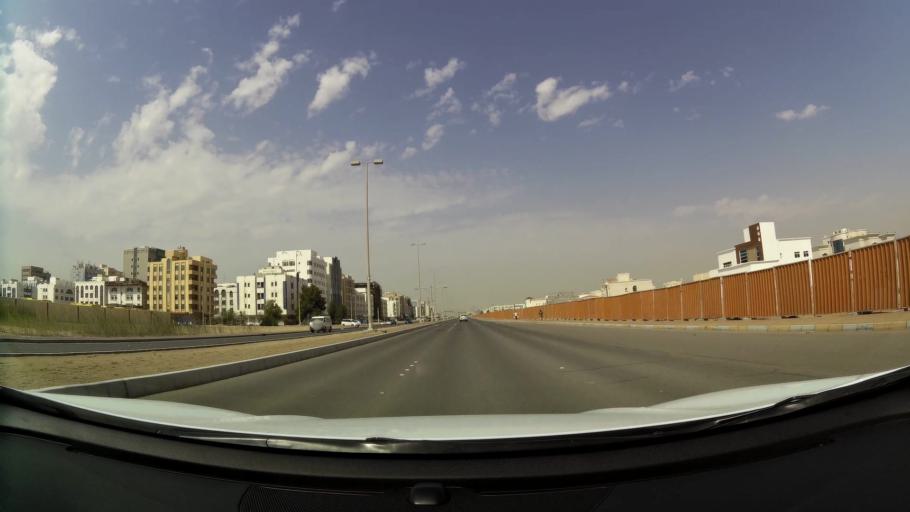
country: AE
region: Abu Dhabi
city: Abu Dhabi
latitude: 24.3329
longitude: 54.5388
